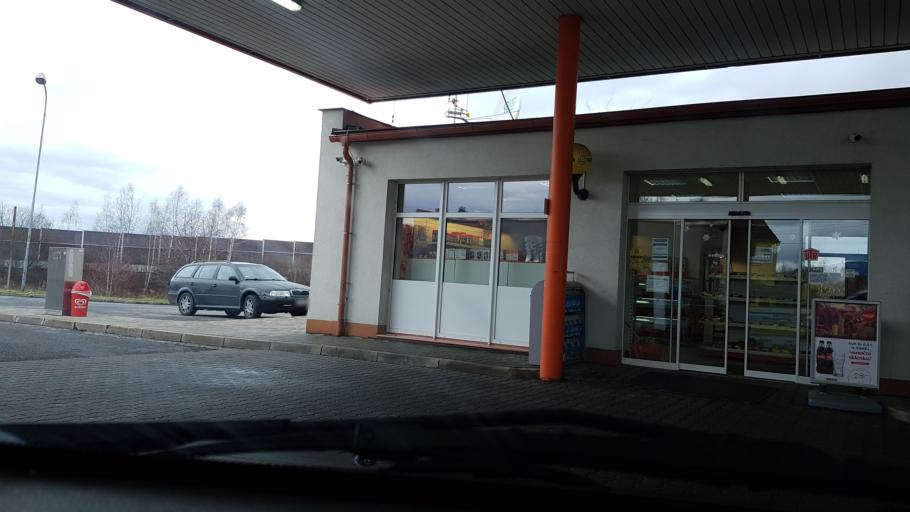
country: CZ
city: Dobra
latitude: 49.6720
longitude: 18.4263
